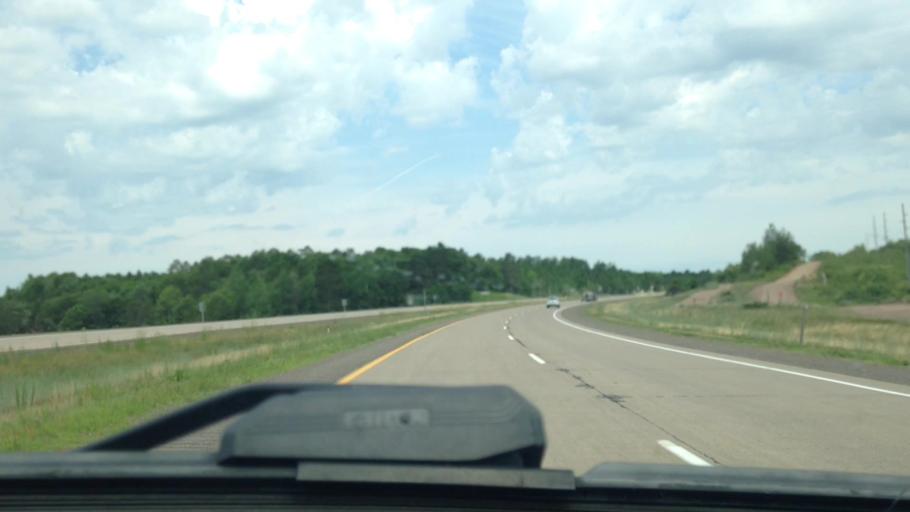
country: US
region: Wisconsin
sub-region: Douglas County
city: Lake Nebagamon
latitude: 46.2178
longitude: -91.7990
